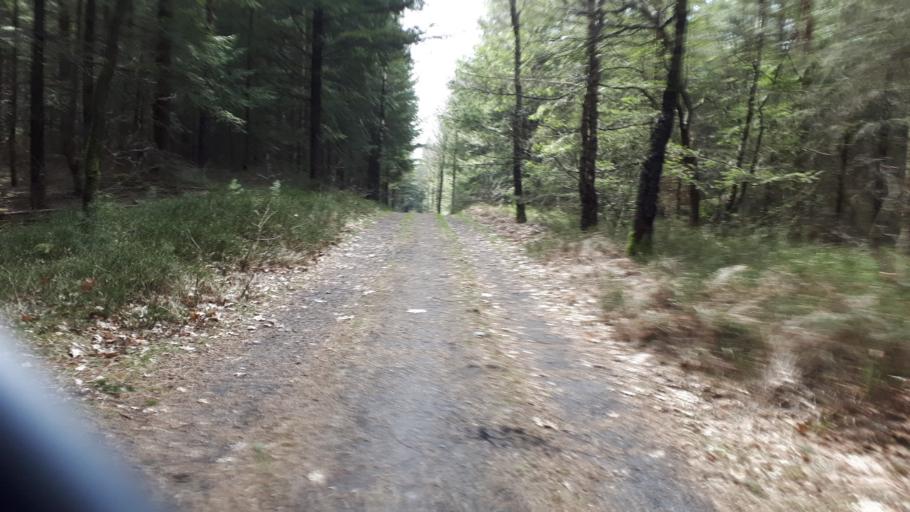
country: DE
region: Lower Saxony
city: Grossenkneten
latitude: 53.0158
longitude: 8.2924
